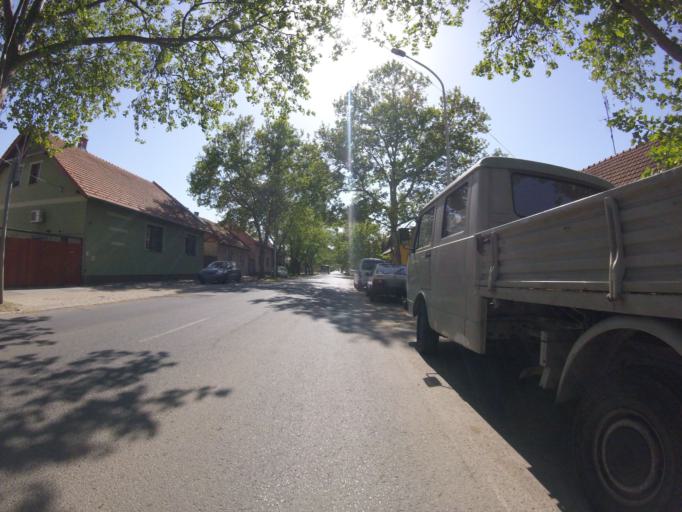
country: HU
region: Jasz-Nagykun-Szolnok
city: Szolnok
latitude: 47.1737
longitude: 20.2010
